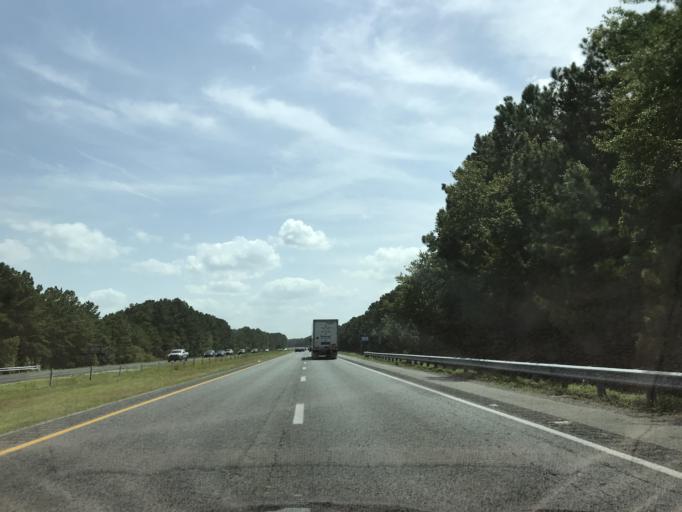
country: US
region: North Carolina
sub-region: Duplin County
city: Wallace
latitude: 34.7183
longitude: -77.9454
